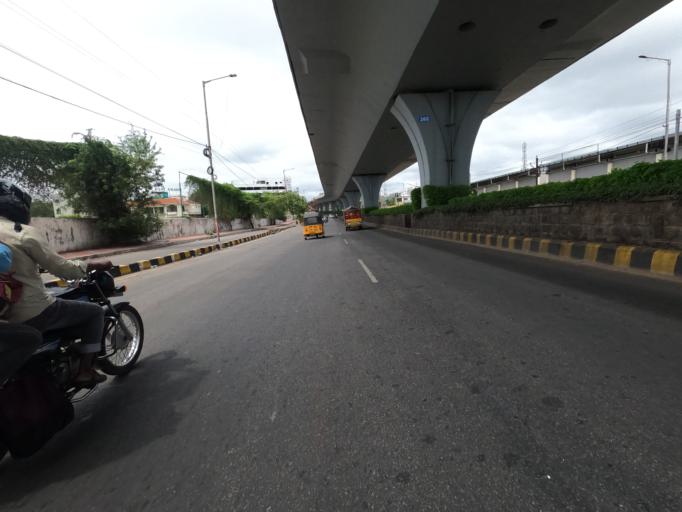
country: IN
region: Telangana
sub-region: Hyderabad
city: Hyderabad
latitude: 17.3303
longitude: 78.4262
